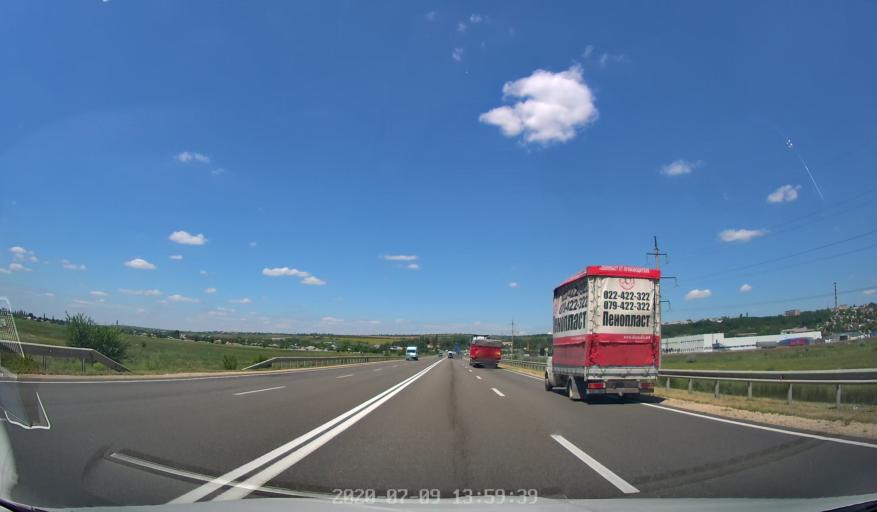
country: MD
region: Orhei
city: Orhei
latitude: 47.3792
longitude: 28.7962
